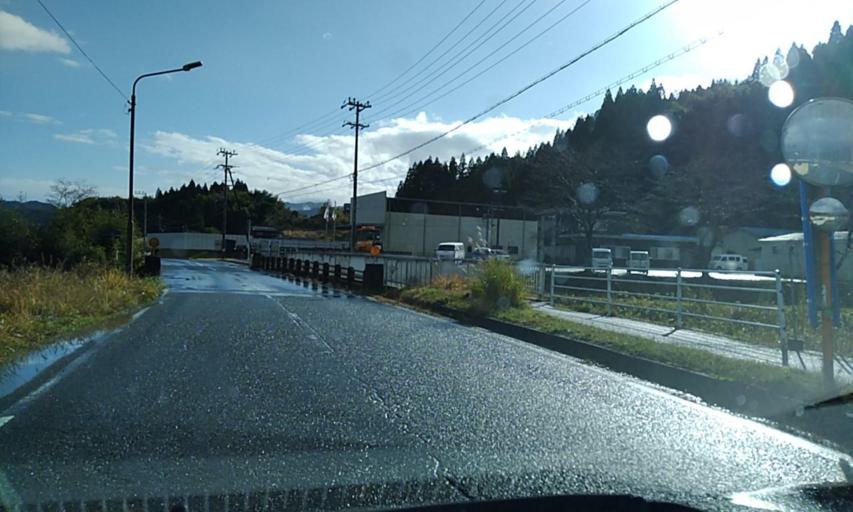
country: JP
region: Kyoto
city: Fukuchiyama
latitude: 35.3995
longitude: 135.1483
